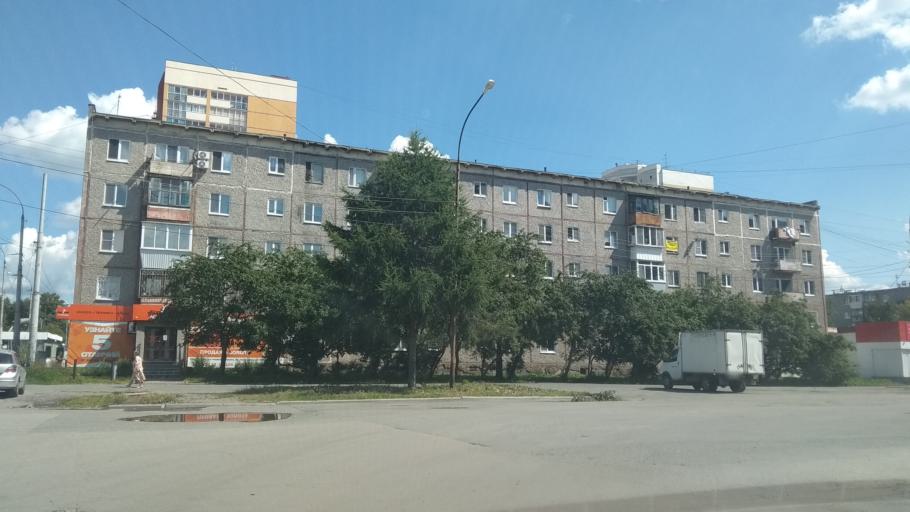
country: RU
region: Sverdlovsk
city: Yekaterinburg
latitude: 56.8347
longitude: 60.6896
